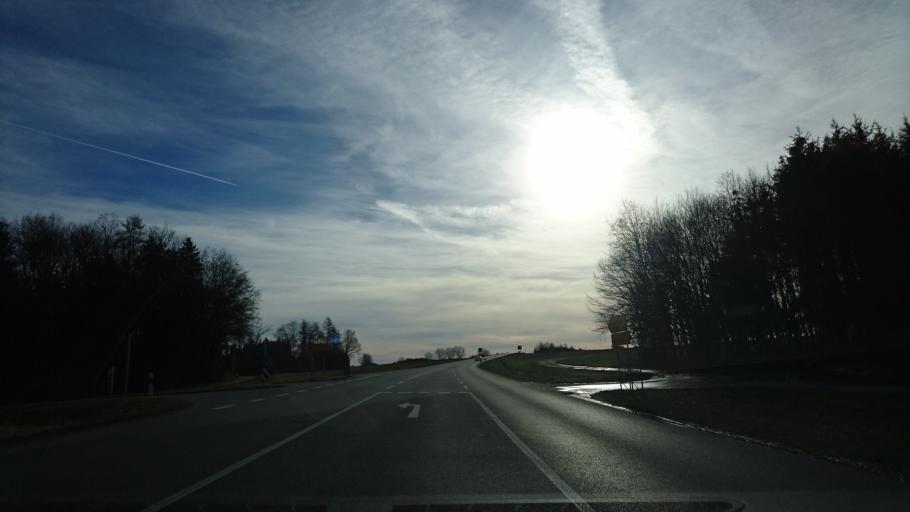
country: DE
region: Bavaria
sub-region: Swabia
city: Biberbach
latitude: 48.5252
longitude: 10.7854
